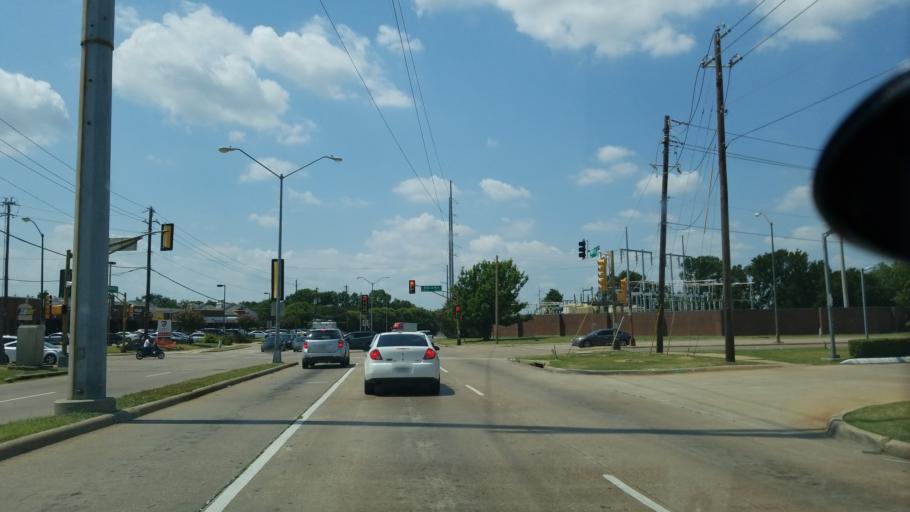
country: US
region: Texas
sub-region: Dallas County
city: Richardson
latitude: 32.9242
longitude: -96.7355
